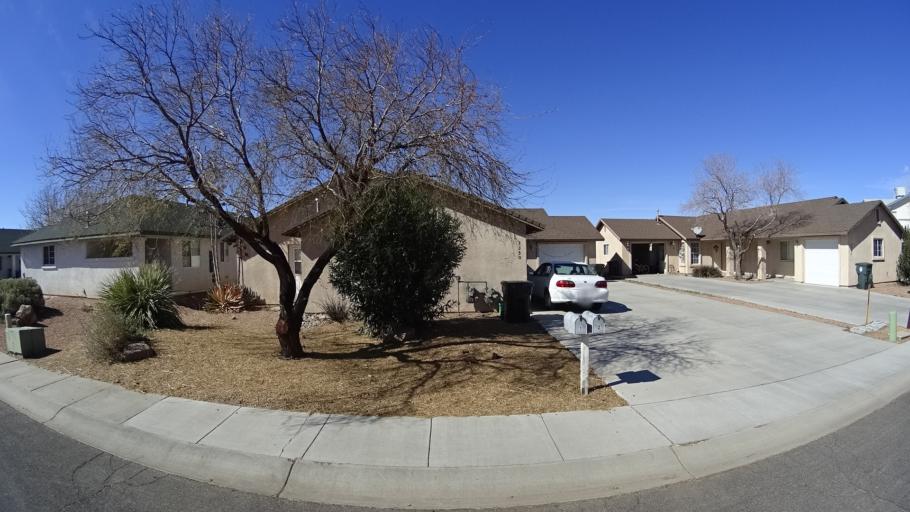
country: US
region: Arizona
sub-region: Mohave County
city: Kingman
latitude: 35.2208
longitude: -114.0222
